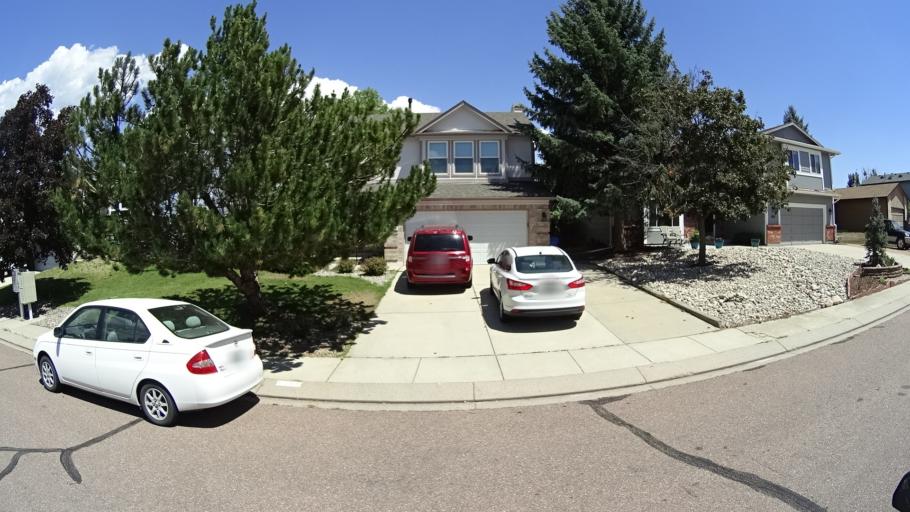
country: US
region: Colorado
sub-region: El Paso County
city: Black Forest
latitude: 38.9500
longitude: -104.7481
